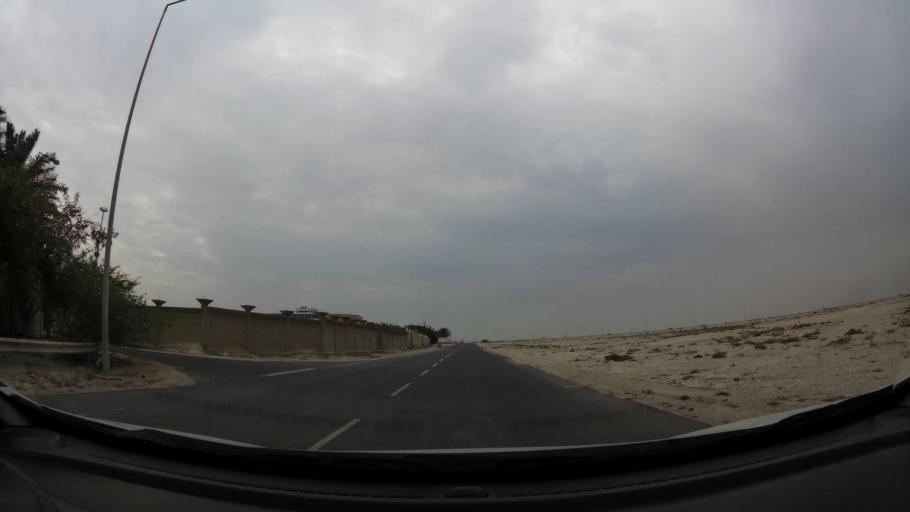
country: BH
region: Northern
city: Ar Rifa'
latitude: 26.0612
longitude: 50.6147
